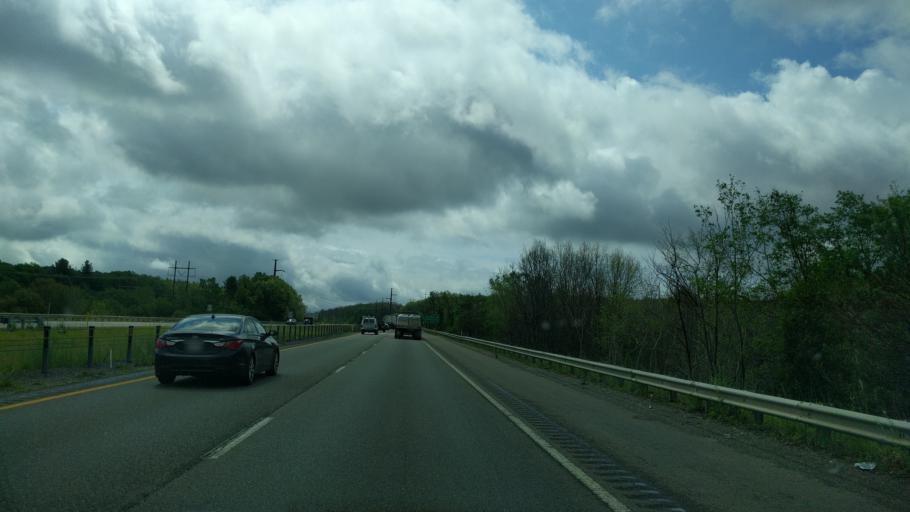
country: US
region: Massachusetts
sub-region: Worcester County
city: Sutton
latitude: 42.1442
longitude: -71.7173
